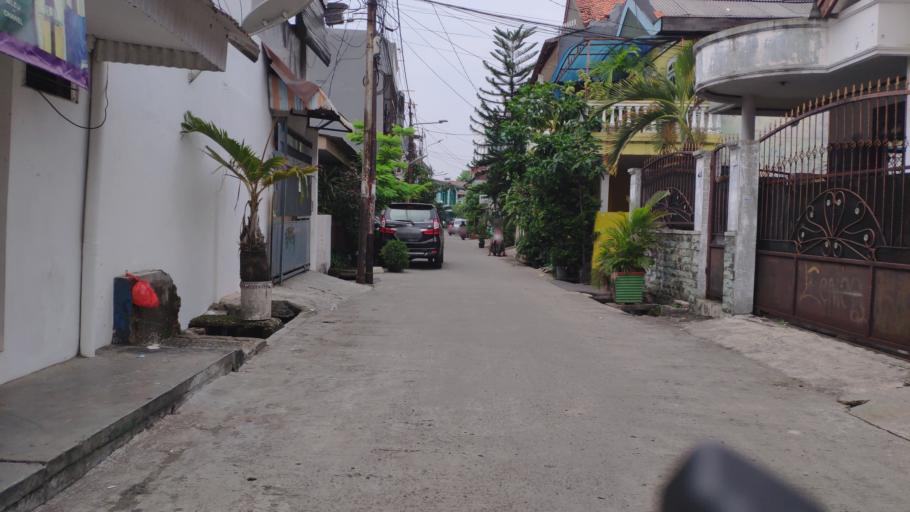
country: ID
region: Jakarta Raya
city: Jakarta
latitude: -6.2196
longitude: 106.8432
